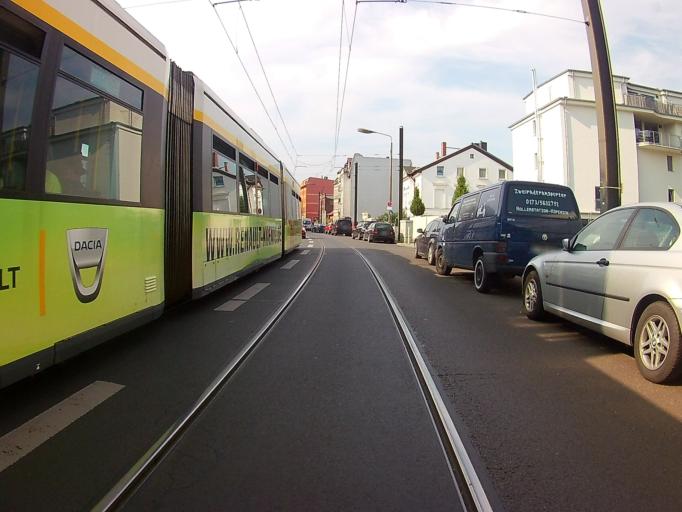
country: DE
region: Berlin
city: Kopenick Bezirk
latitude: 52.4381
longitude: 13.5717
